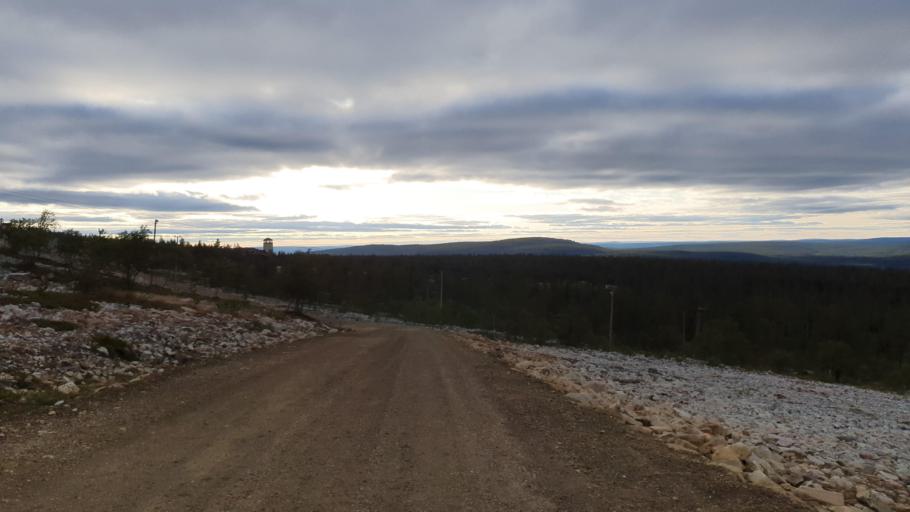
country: FI
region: Lapland
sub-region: Tunturi-Lappi
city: Kolari
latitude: 67.5799
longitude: 24.2185
